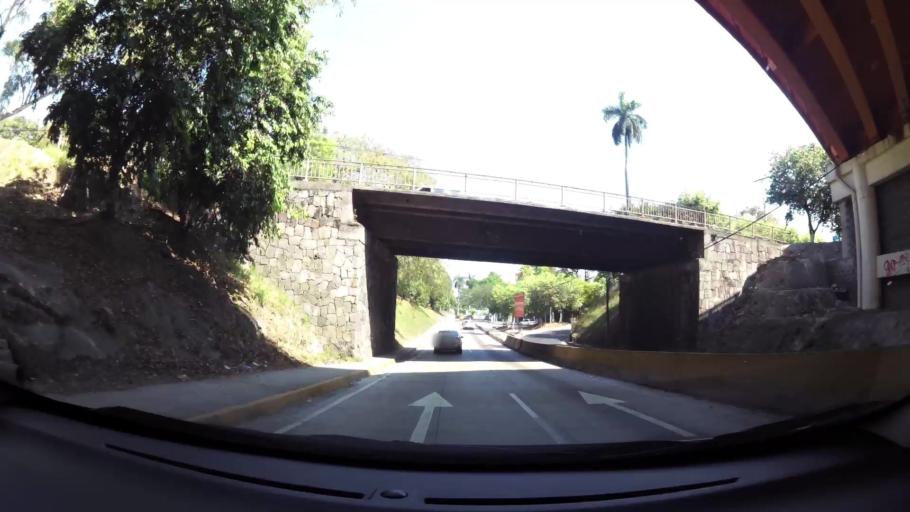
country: SV
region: La Libertad
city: Antiguo Cuscatlan
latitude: 13.6837
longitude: -89.2396
